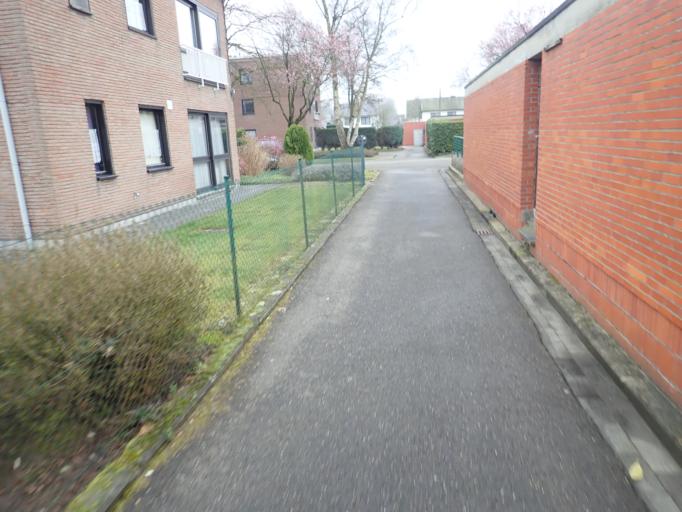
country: BE
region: Flanders
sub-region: Provincie Antwerpen
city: Essen
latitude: 51.4619
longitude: 4.4594
